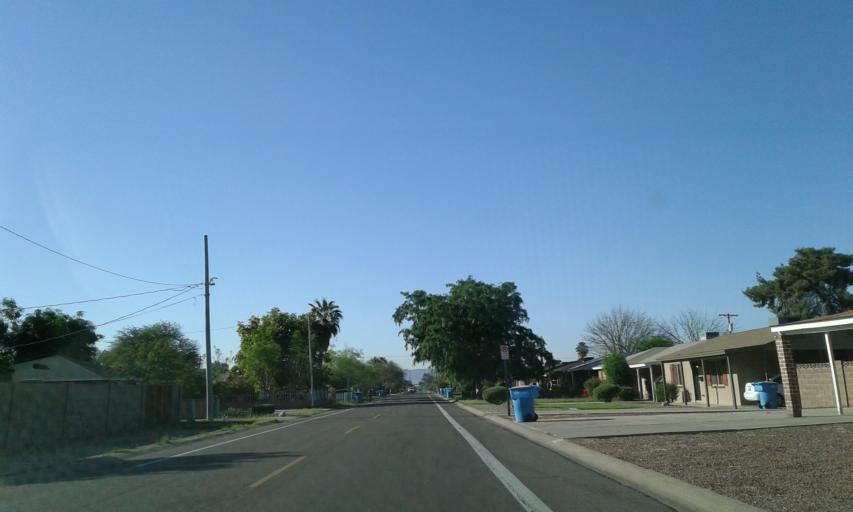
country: US
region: Arizona
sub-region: Maricopa County
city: Phoenix
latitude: 33.4896
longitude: -112.1084
